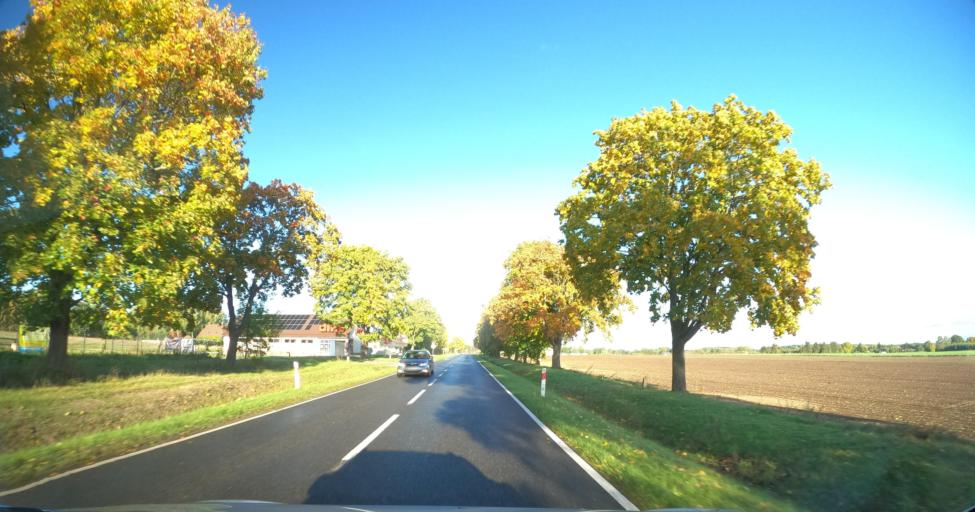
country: PL
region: Lubusz
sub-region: Powiat zielonogorski
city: Zabor
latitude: 51.9288
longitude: 15.6483
